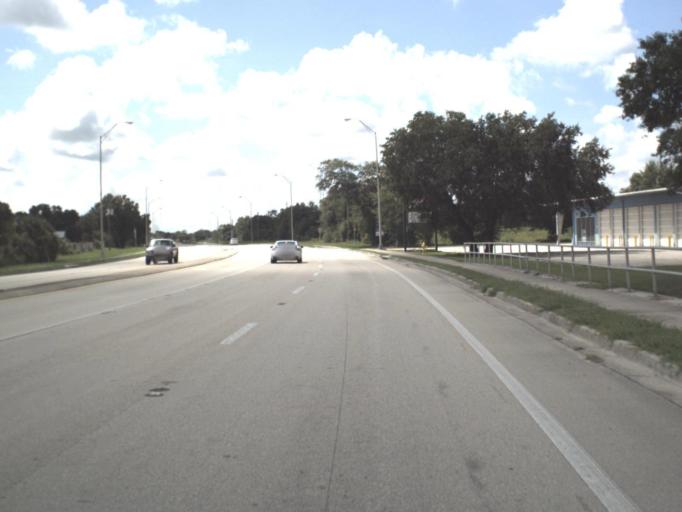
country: US
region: Florida
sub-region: DeSoto County
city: Arcadia
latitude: 27.2384
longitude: -81.8525
